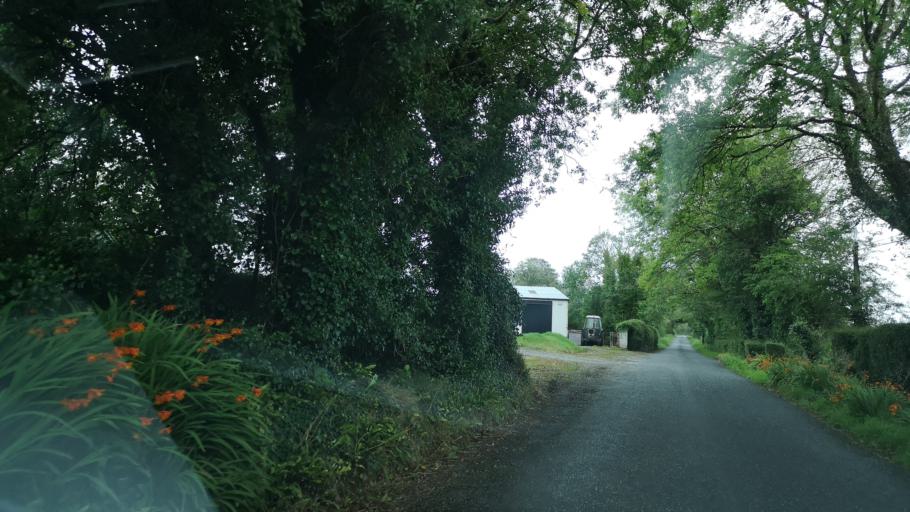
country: IE
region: Connaught
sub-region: County Galway
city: Loughrea
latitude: 53.3035
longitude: -8.6118
